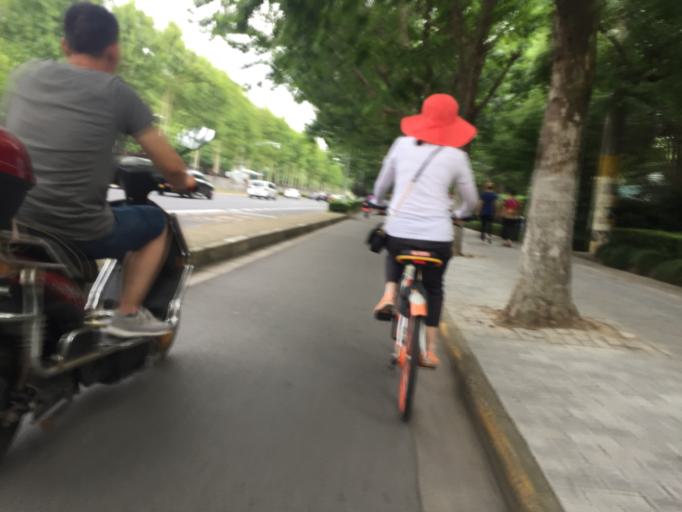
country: CN
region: Shanghai Shi
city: Huamu
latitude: 31.1859
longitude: 121.5365
